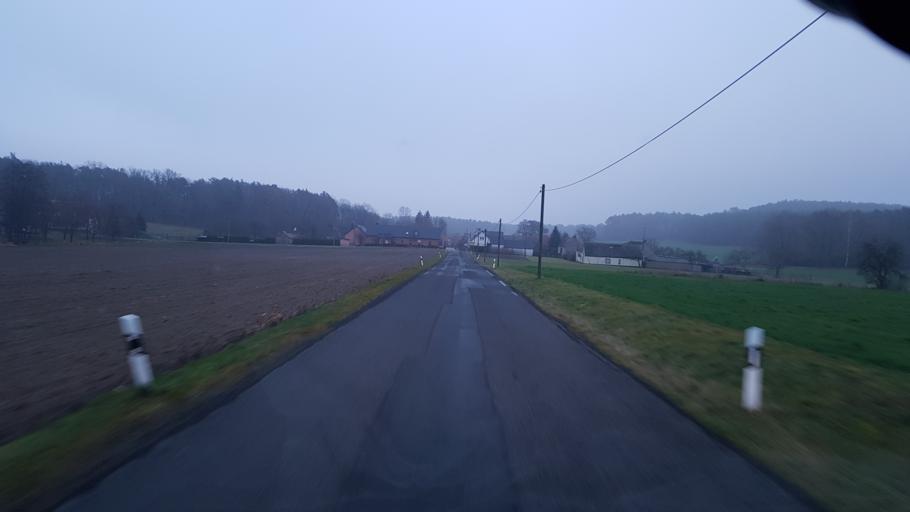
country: DE
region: Brandenburg
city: Bronkow
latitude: 51.6870
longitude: 13.9583
